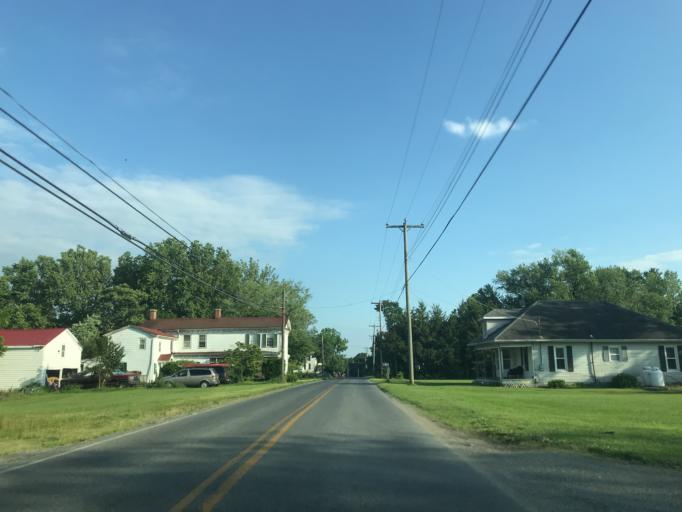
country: US
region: Maryland
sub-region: Caroline County
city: Federalsburg
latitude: 38.7053
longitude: -75.7766
